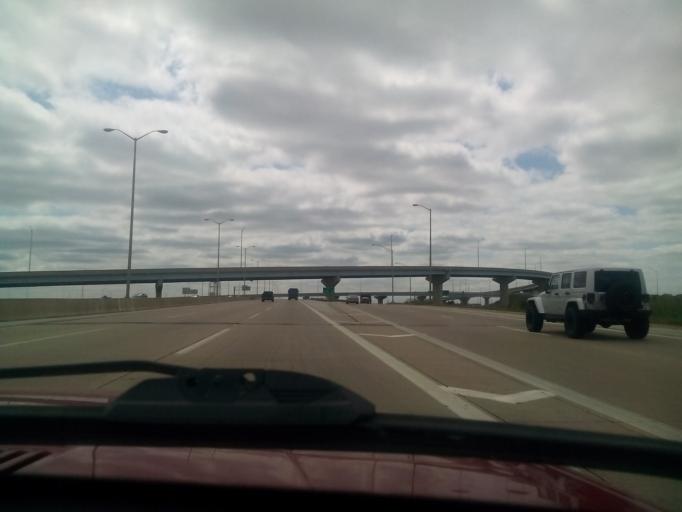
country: US
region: Illinois
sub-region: Will County
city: Bolingbrook
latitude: 41.7091
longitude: -88.0318
